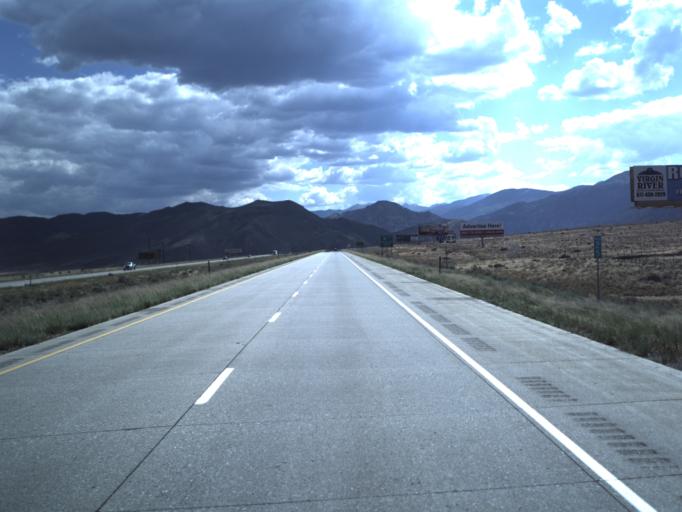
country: US
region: Utah
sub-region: Sevier County
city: Monroe
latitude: 38.6146
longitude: -112.2307
